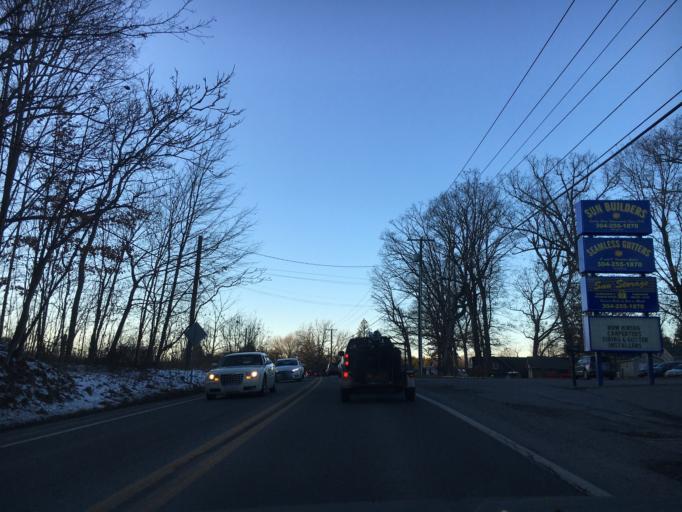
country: US
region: West Virginia
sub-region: Raleigh County
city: Daniels
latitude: 37.7397
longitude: -81.1153
